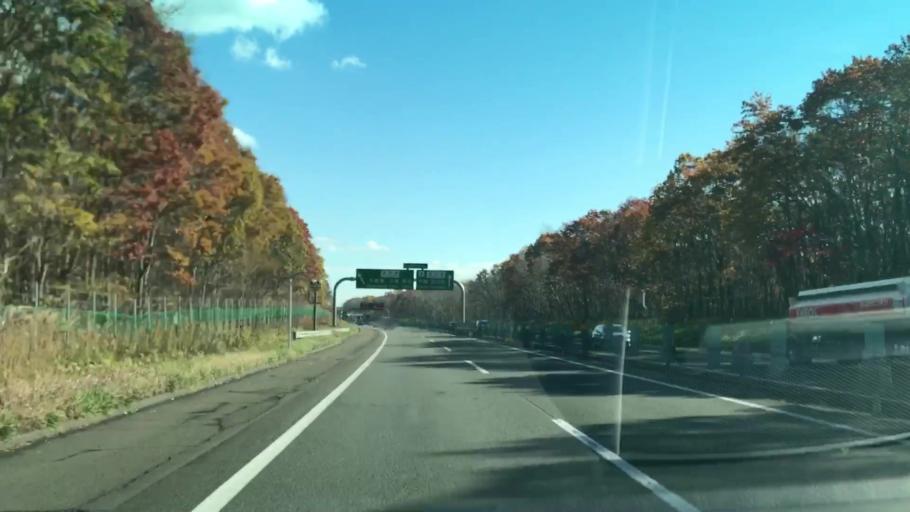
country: JP
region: Hokkaido
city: Chitose
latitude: 42.8506
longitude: 141.5709
